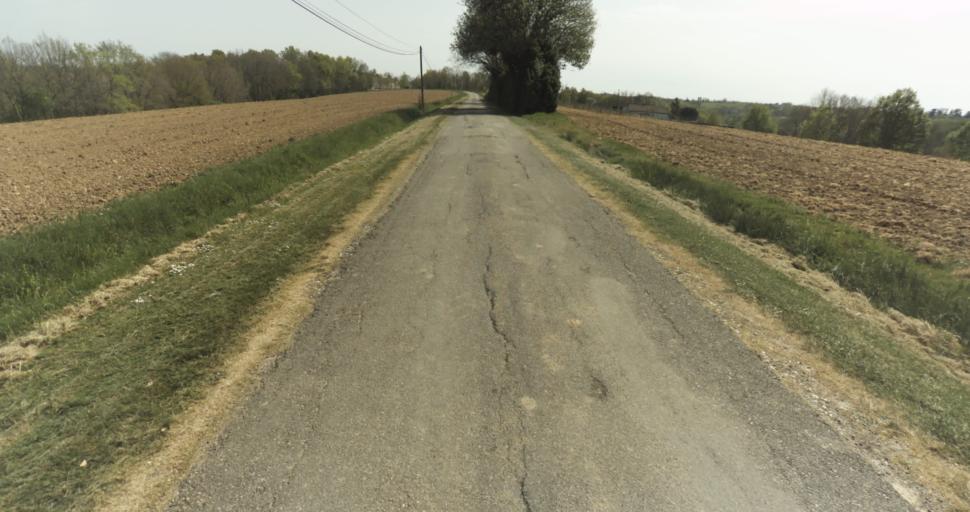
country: FR
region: Midi-Pyrenees
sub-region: Departement du Tarn-et-Garonne
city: Moissac
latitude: 44.1628
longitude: 1.0742
